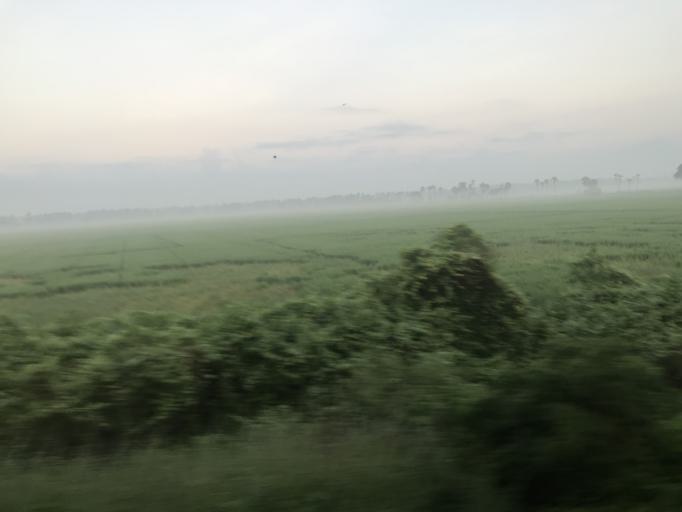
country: IN
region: Andhra Pradesh
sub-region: Guntur
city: Ponnur
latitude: 16.0904
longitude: 80.5677
